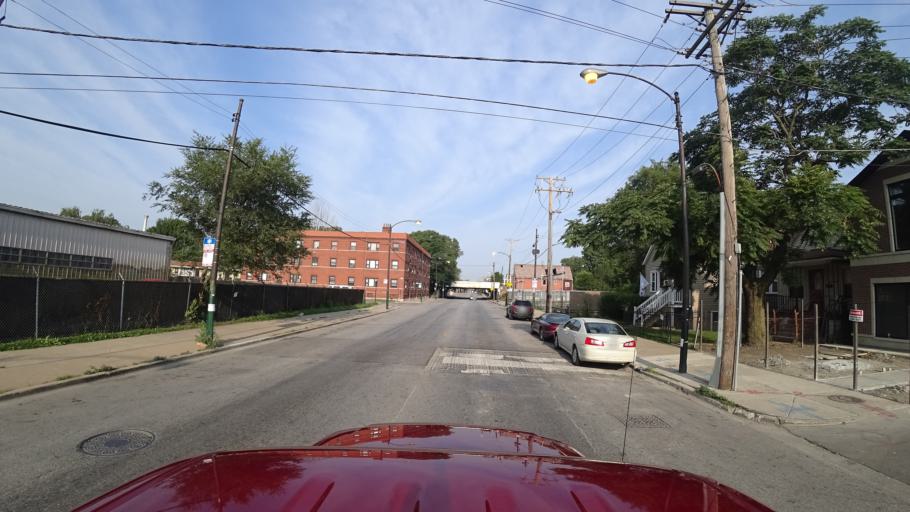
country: US
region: Illinois
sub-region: Cook County
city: Chicago
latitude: 41.8303
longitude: -87.6857
